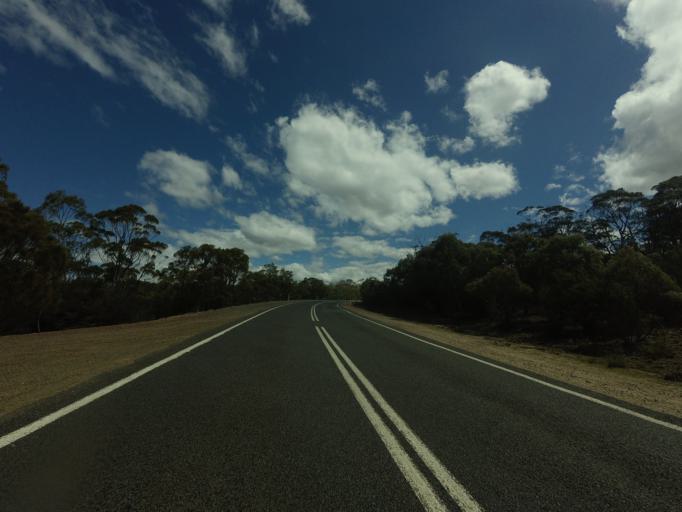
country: AU
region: Tasmania
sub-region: Break O'Day
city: St Helens
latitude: -42.0153
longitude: 147.9587
